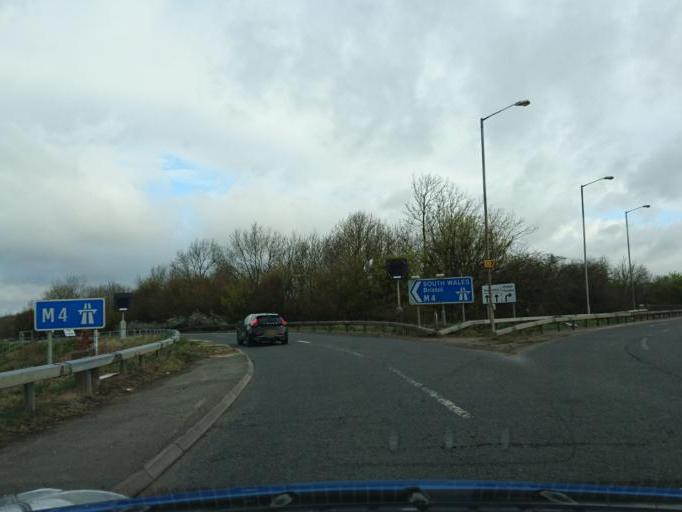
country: GB
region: England
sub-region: Wiltshire
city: Lydiard Tregoze
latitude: 51.5448
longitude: -1.8552
